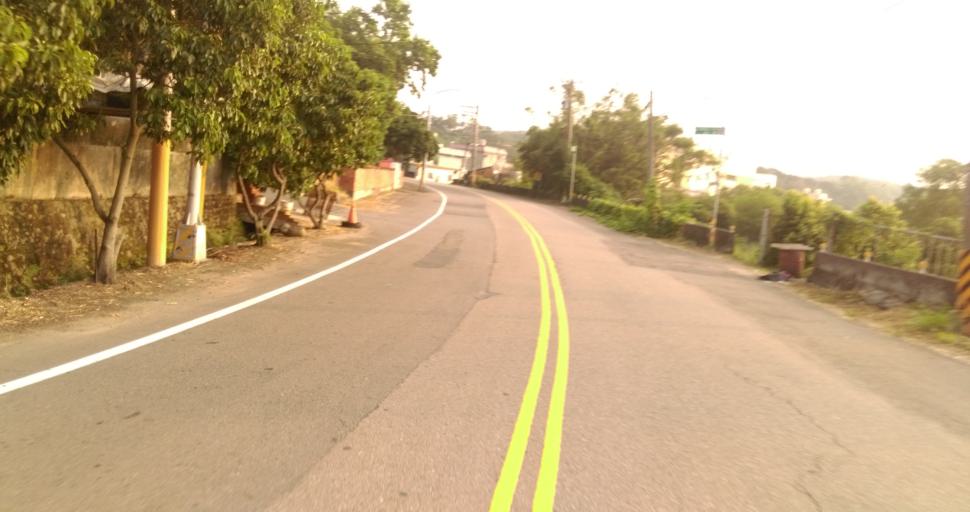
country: TW
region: Taiwan
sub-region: Hsinchu
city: Hsinchu
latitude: 24.7491
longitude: 120.9375
